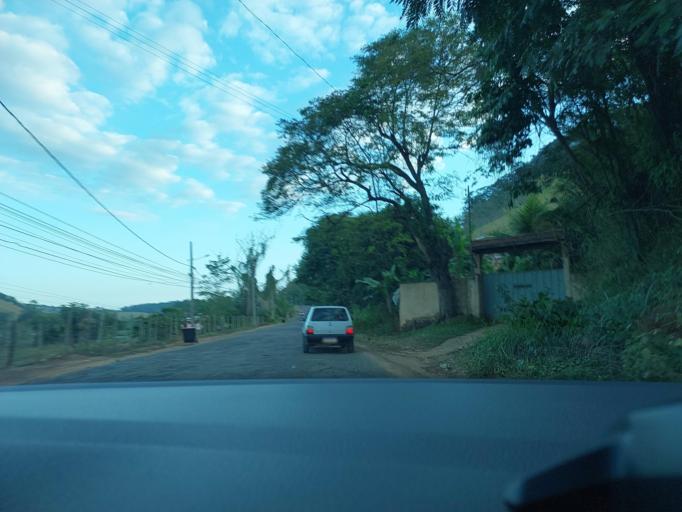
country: BR
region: Rio de Janeiro
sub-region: Natividade
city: Natividade
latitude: -21.1831
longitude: -42.1035
